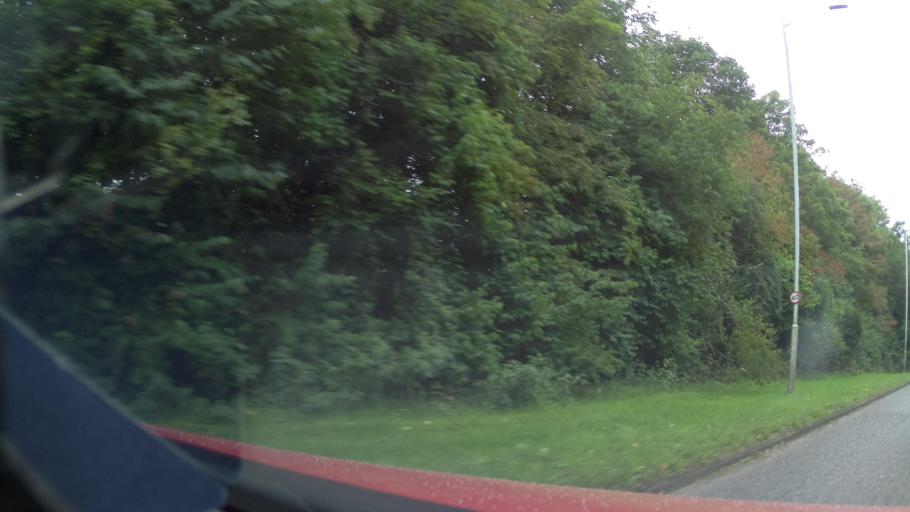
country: GB
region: Scotland
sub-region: Fife
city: Glenrothes
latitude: 56.1992
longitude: -3.1787
